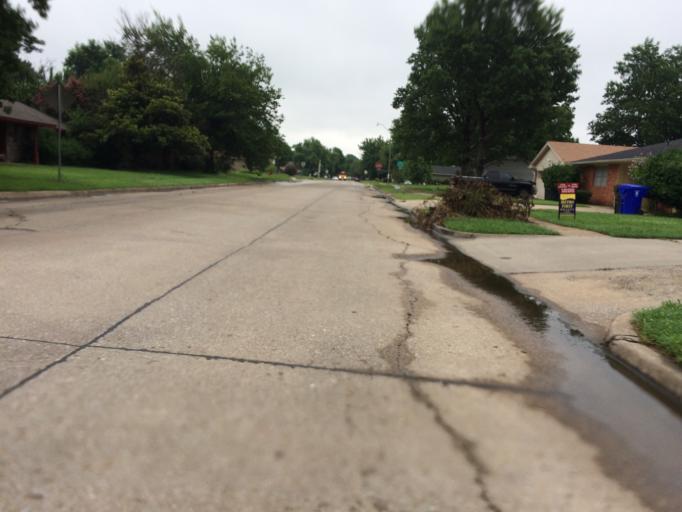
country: US
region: Oklahoma
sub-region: Cleveland County
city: Norman
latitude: 35.2115
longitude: -97.4209
